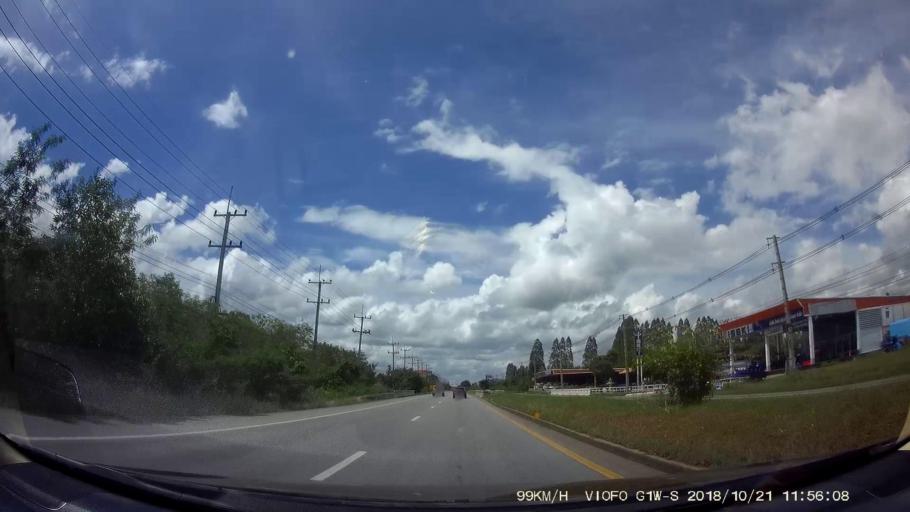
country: TH
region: Chaiyaphum
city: Chatturat
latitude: 15.5781
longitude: 101.8802
